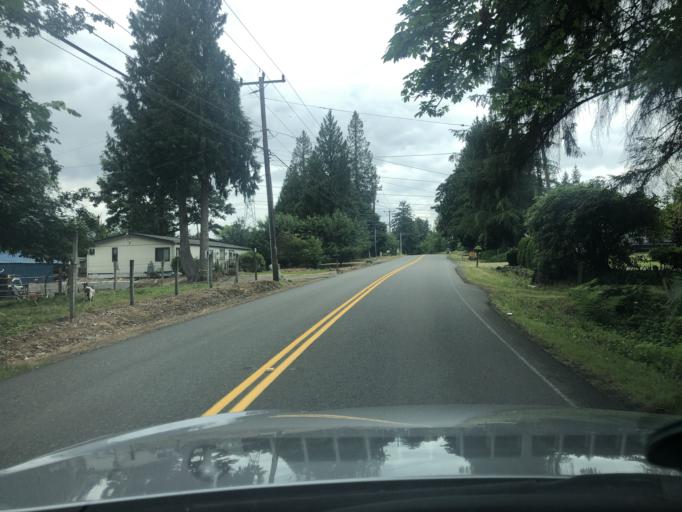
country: US
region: Washington
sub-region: King County
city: Lake Morton-Berrydale
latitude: 47.3267
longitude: -122.0911
